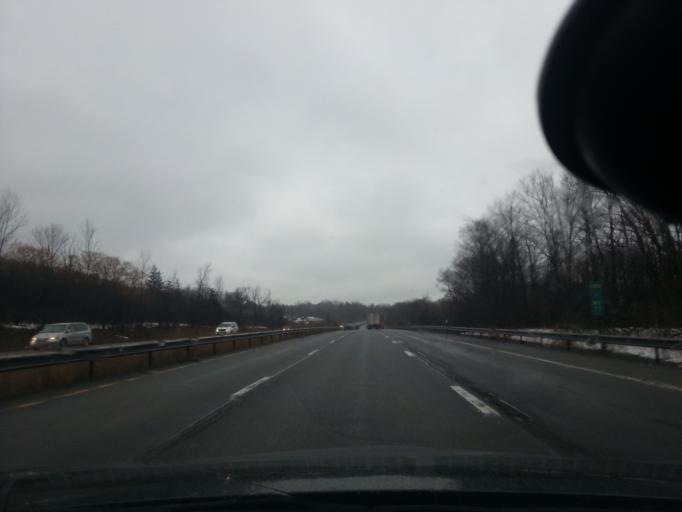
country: US
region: New York
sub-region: Onondaga County
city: Nedrow
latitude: 42.9363
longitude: -76.1312
